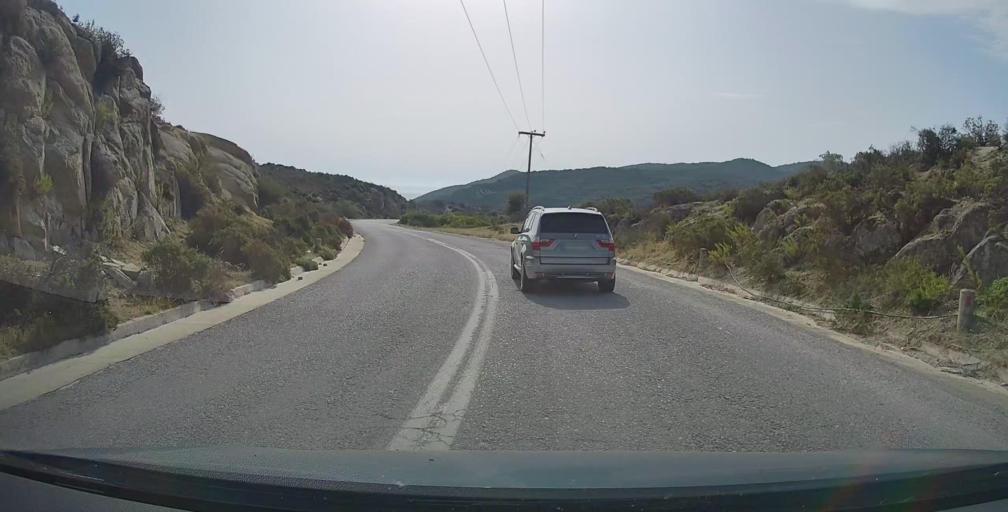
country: GR
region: Central Macedonia
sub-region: Nomos Chalkidikis
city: Sykia
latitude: 39.9894
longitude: 23.9698
